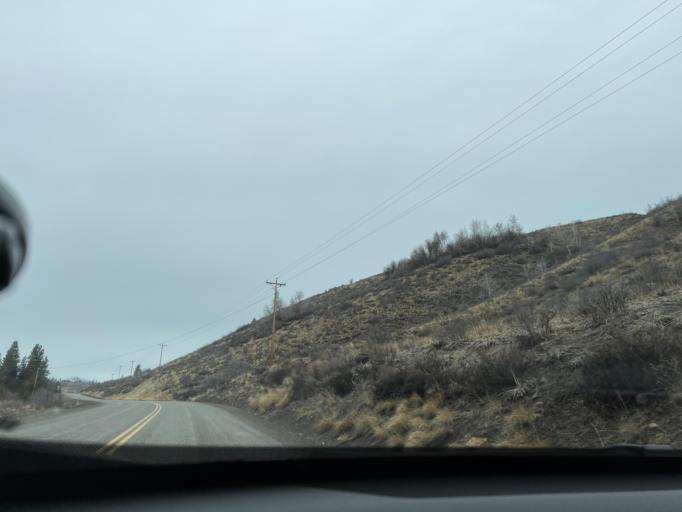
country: US
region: Washington
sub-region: Chelan County
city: Granite Falls
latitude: 48.4498
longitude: -120.2393
